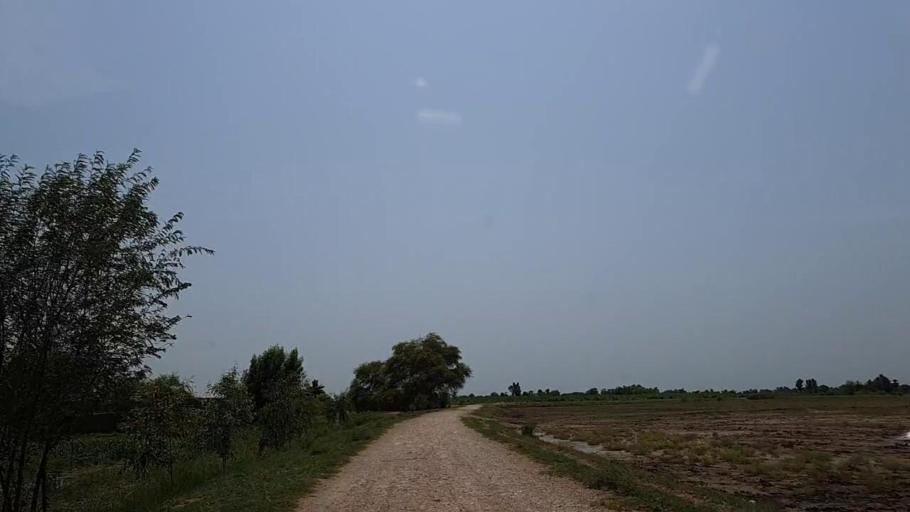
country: PK
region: Sindh
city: Ghotki
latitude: 27.9883
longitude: 69.4083
